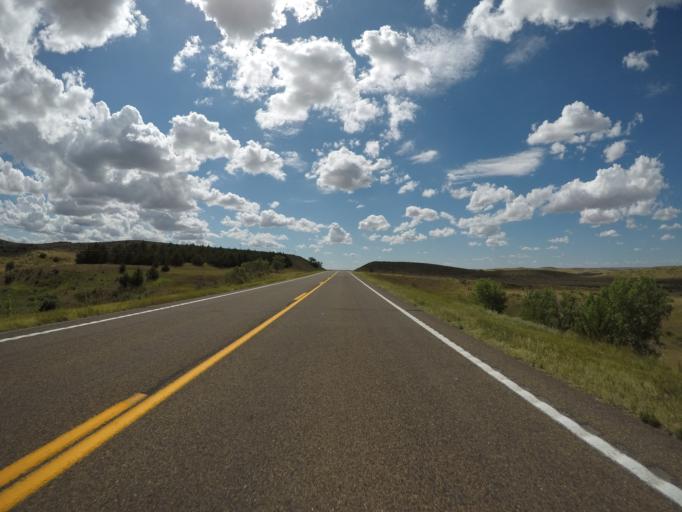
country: US
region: Nebraska
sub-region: Chase County
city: Imperial
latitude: 40.4163
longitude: -101.4203
